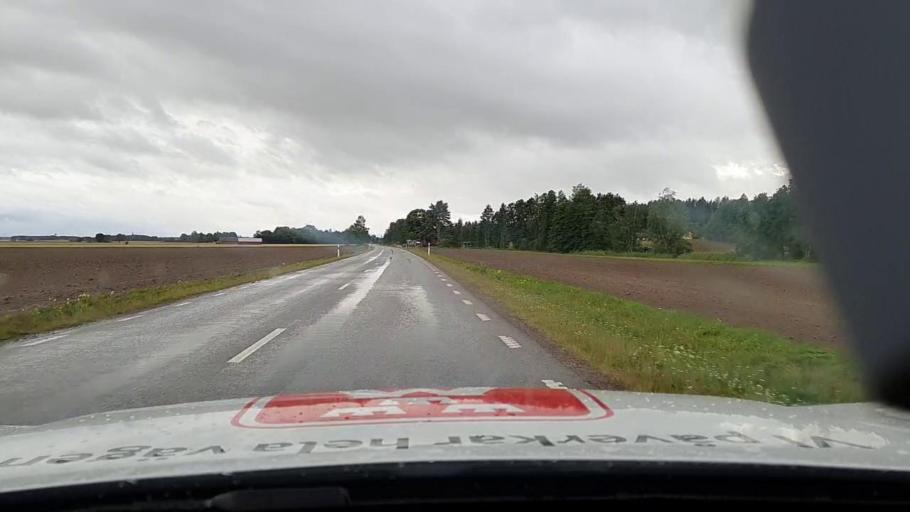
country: SE
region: Vaestra Goetaland
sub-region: Toreboda Kommun
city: Toereboda
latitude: 58.6323
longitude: 14.0206
